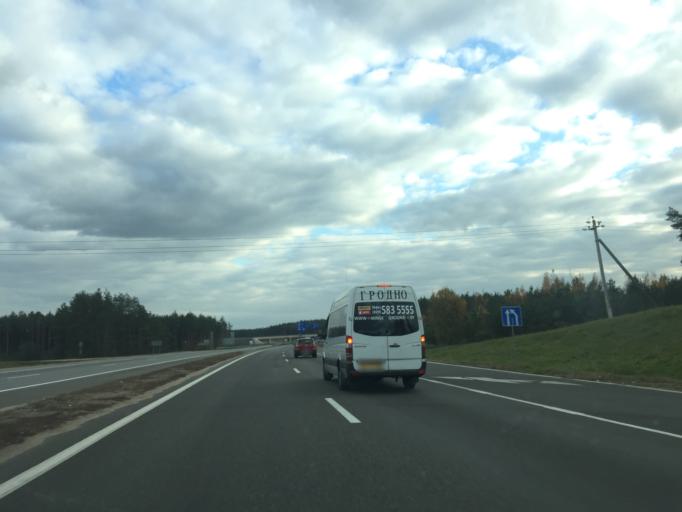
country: BY
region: Minsk
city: Rakaw
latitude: 53.9707
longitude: 27.0807
